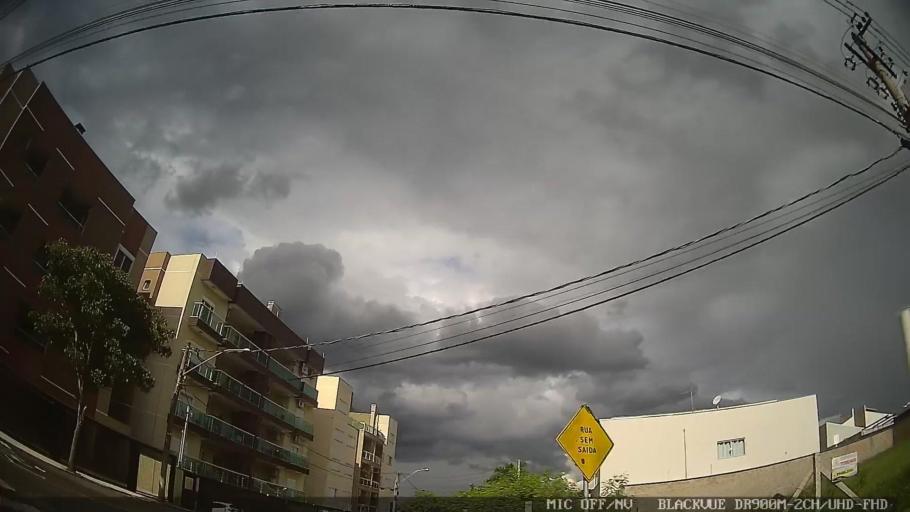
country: BR
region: Sao Paulo
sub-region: Jaguariuna
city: Jaguariuna
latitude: -22.6933
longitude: -46.9828
